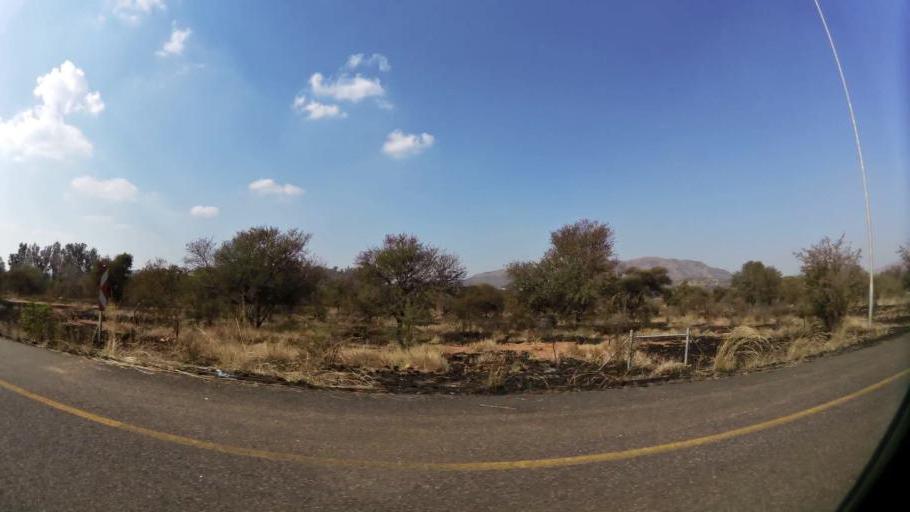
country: ZA
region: North-West
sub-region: Bojanala Platinum District Municipality
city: Rustenburg
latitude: -25.6305
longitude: 27.1576
